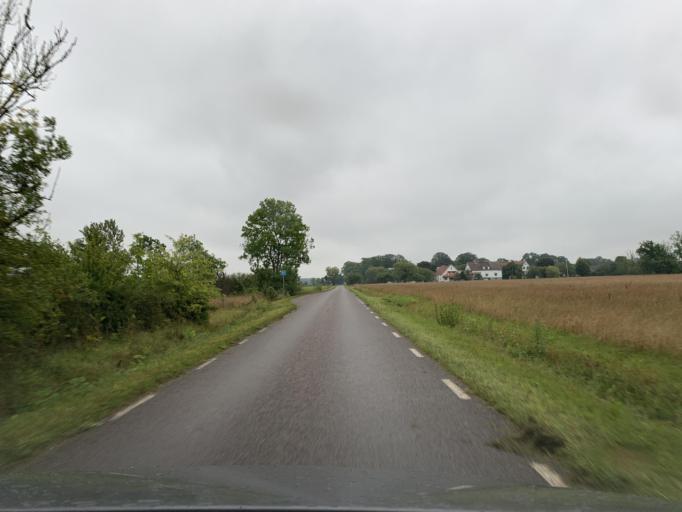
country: SE
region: Gotland
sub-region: Gotland
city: Visby
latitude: 57.6040
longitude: 18.5215
